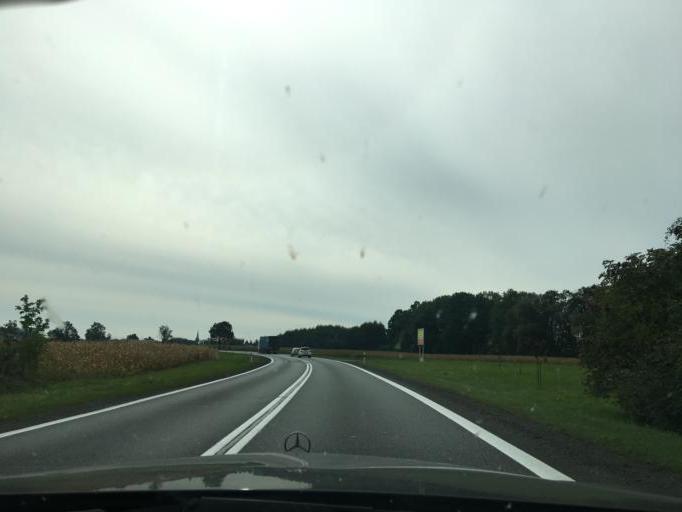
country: PL
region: Lower Silesian Voivodeship
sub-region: Powiat wroclawski
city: Jordanow Slaski
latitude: 50.8771
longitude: 16.8592
